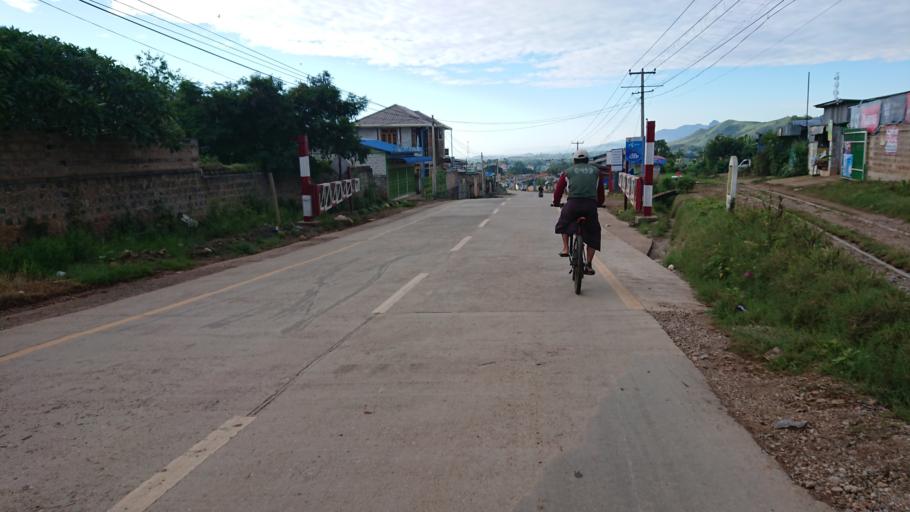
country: MM
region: Shan
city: Taunggyi
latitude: 20.7443
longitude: 97.0507
